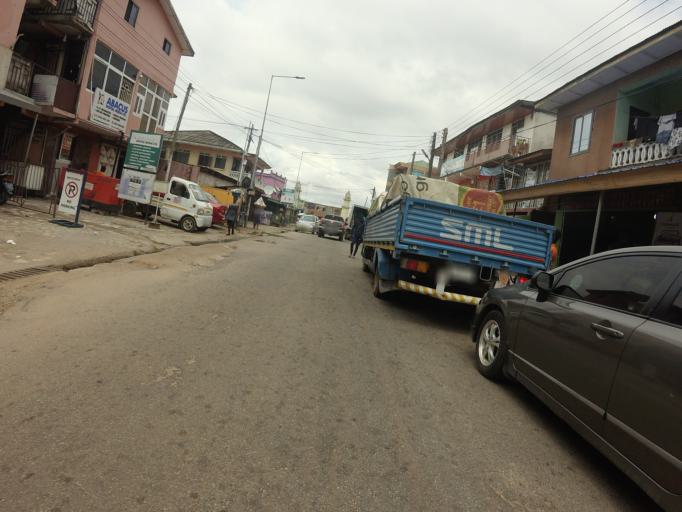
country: GH
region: Greater Accra
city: Accra
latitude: 5.5817
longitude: -0.2079
